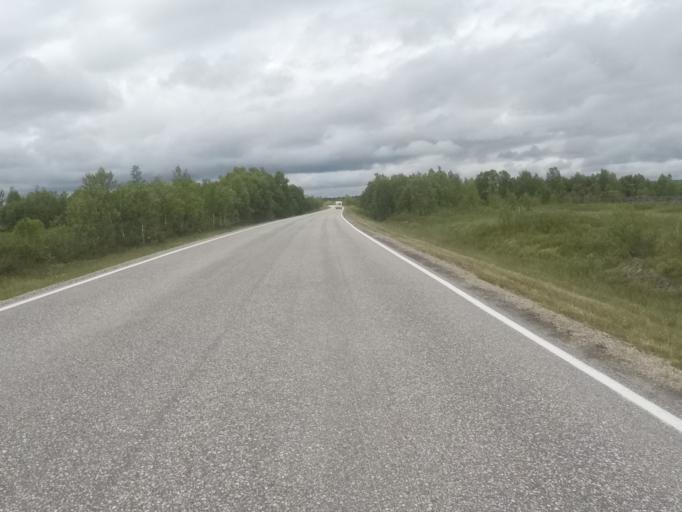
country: FI
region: Lapland
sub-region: Tunturi-Lappi
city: Enontekioe
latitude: 68.4840
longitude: 23.3585
